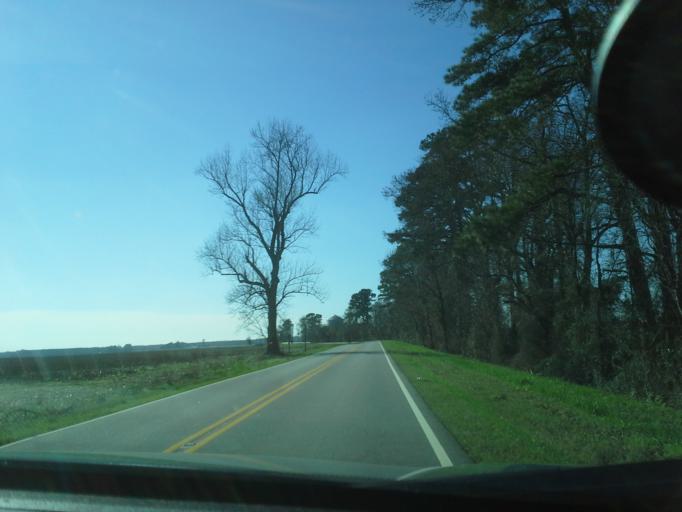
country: US
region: North Carolina
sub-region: Beaufort County
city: Belhaven
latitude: 35.6210
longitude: -76.6418
